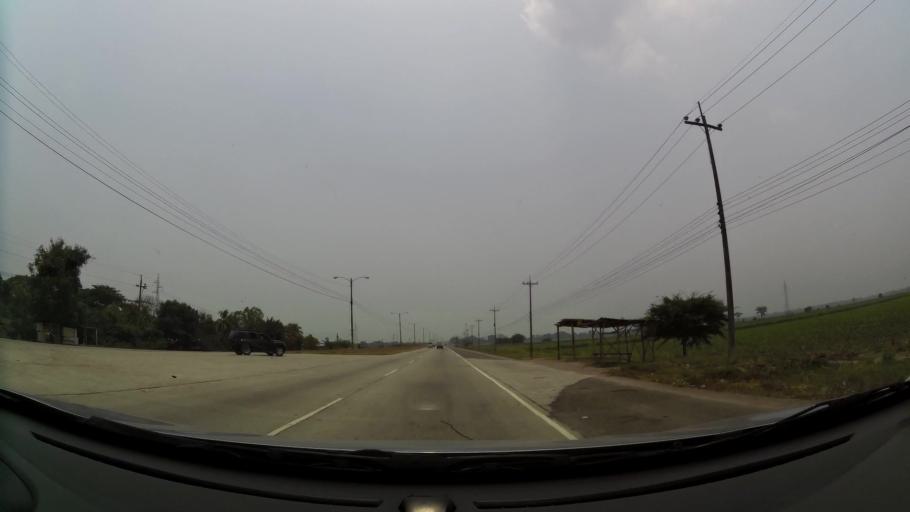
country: HN
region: Cortes
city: La Lima
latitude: 15.4117
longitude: -87.8626
